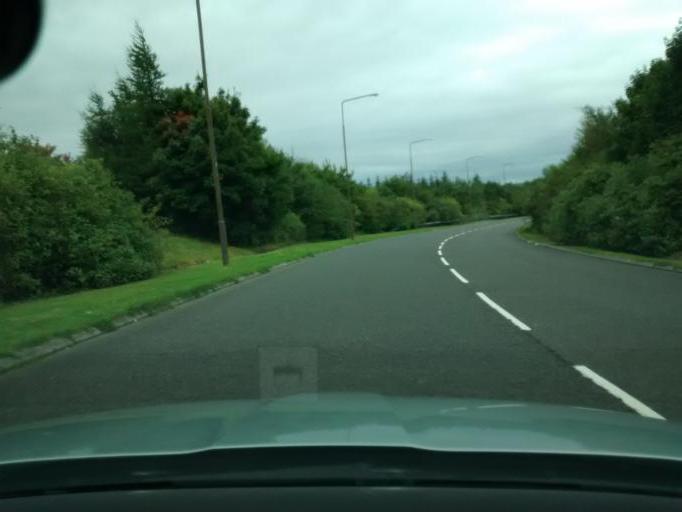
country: GB
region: Scotland
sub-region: West Lothian
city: Livingston
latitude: 55.8929
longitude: -3.5591
